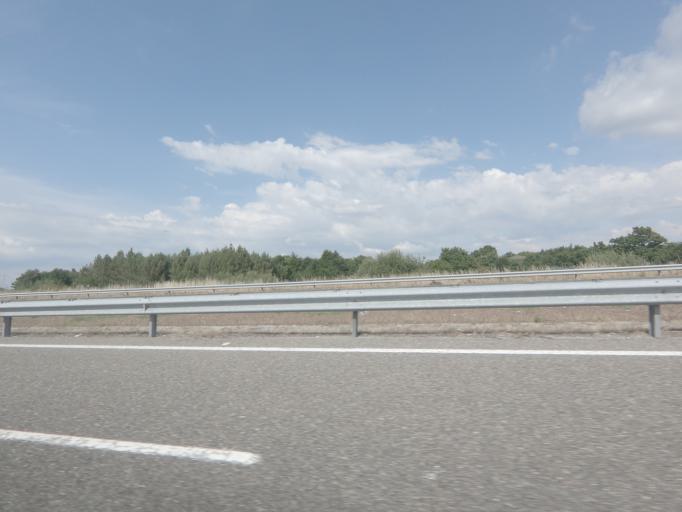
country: ES
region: Galicia
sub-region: Provincia de Ourense
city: Taboadela
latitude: 42.2643
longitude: -7.8689
